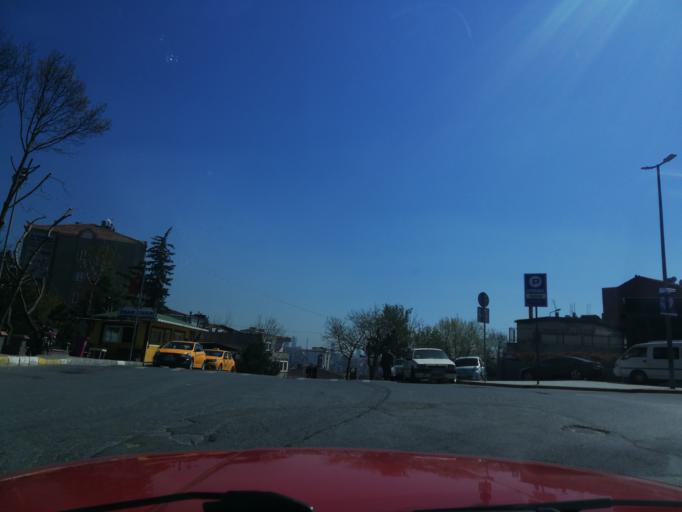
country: TR
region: Istanbul
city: Sisli
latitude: 41.0800
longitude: 28.9378
